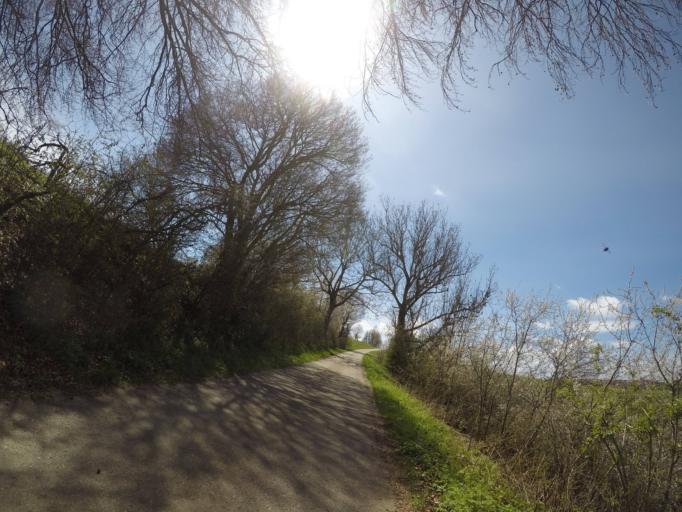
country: DE
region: Baden-Wuerttemberg
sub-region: Regierungsbezirk Stuttgart
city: Neidlingen
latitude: 48.5249
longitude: 9.5670
